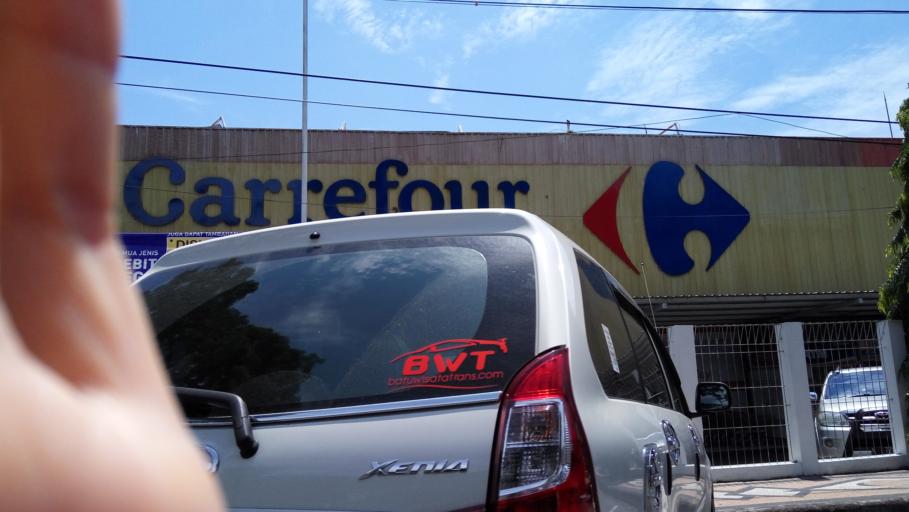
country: ID
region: East Java
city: Malang
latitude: -7.9446
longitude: 112.6412
